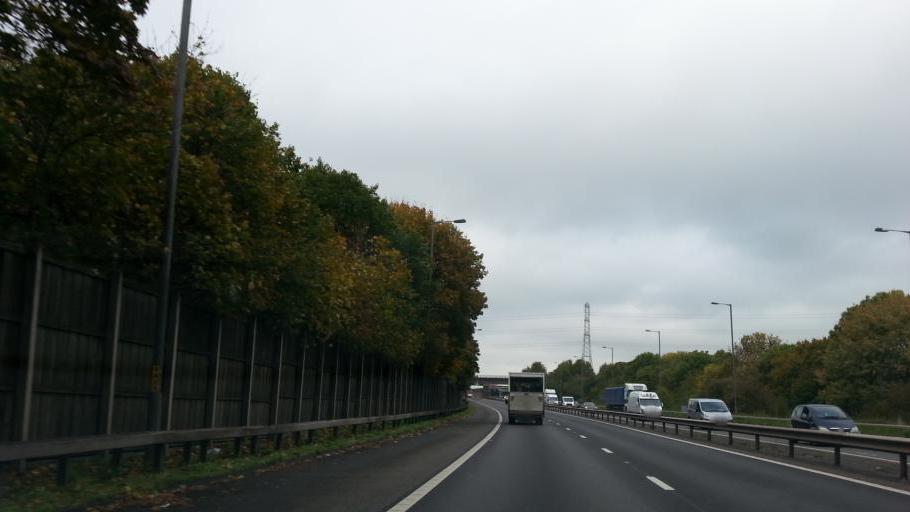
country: GB
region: England
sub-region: Sandwell
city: West Bromwich
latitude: 52.5486
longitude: -1.9687
